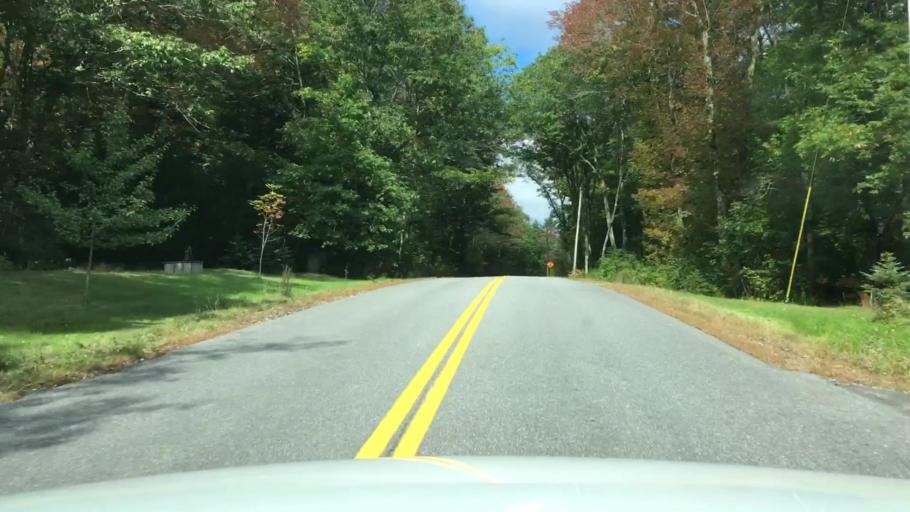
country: US
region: Maine
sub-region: Cumberland County
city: Brunswick
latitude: 43.9663
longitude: -69.8976
